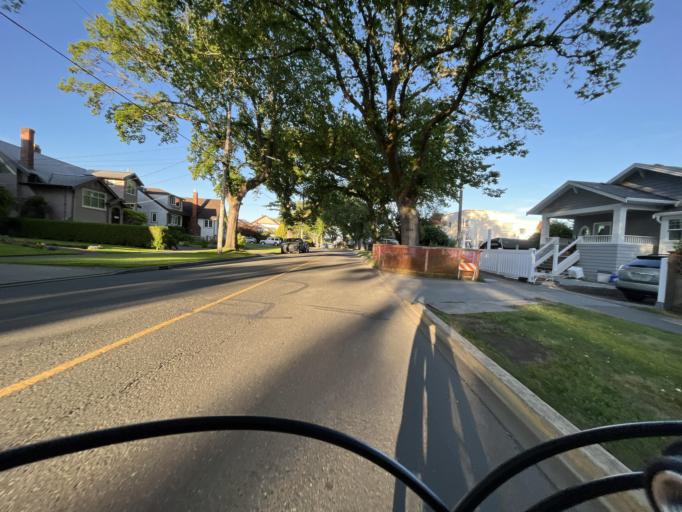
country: CA
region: British Columbia
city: Victoria
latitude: 48.4088
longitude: -123.3337
